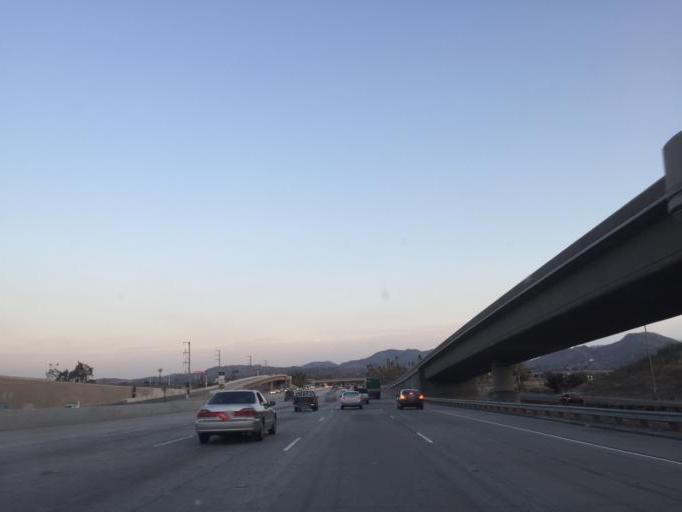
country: US
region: California
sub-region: San Bernardino County
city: Colton
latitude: 34.0837
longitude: -117.3003
